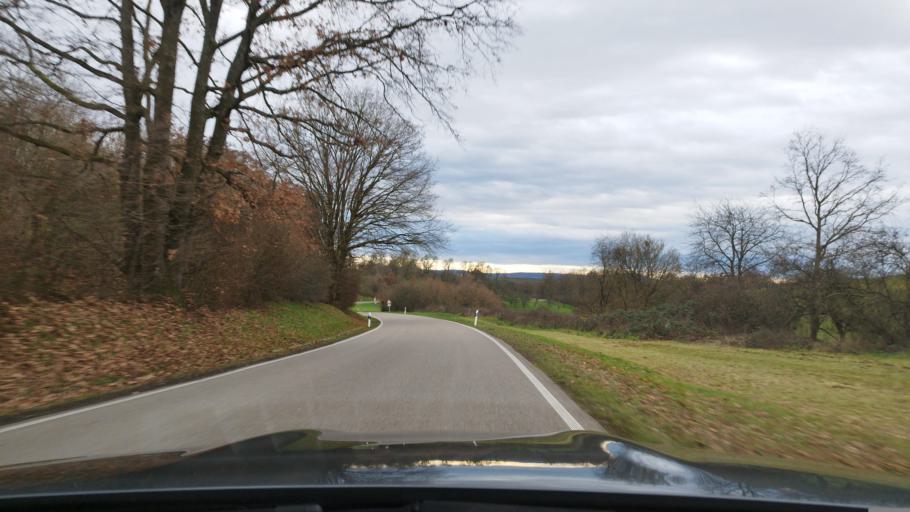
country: DE
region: Baden-Wuerttemberg
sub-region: Regierungsbezirk Stuttgart
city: Kirchberg an der Murr
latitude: 48.9405
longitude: 9.3582
